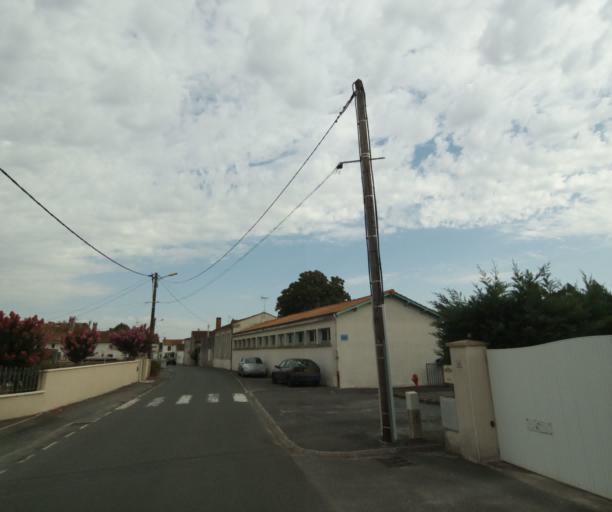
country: FR
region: Poitou-Charentes
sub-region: Departement de la Charente-Maritime
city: Tonnay-Charente
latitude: 45.9651
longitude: -0.8721
